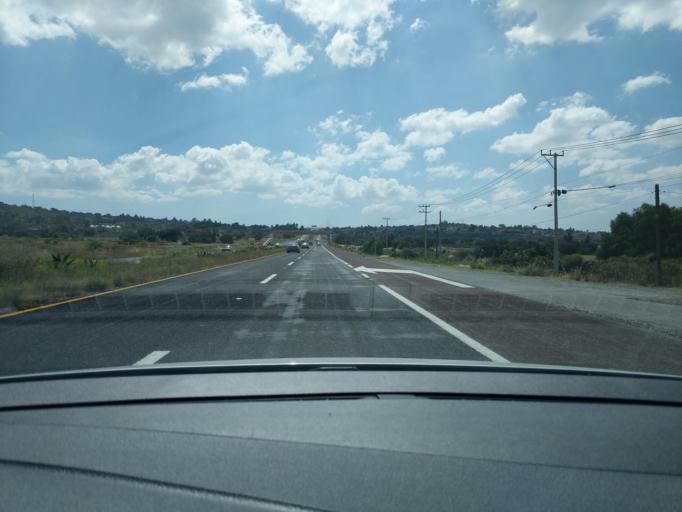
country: MX
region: Hidalgo
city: Zempoala
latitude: 19.9301
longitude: -98.6835
